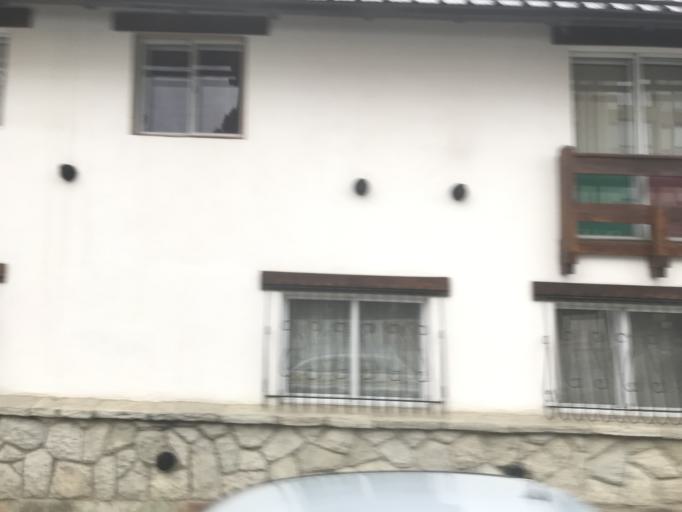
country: AR
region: Rio Negro
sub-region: Departamento de Bariloche
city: San Carlos de Bariloche
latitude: -41.1381
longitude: -71.3148
